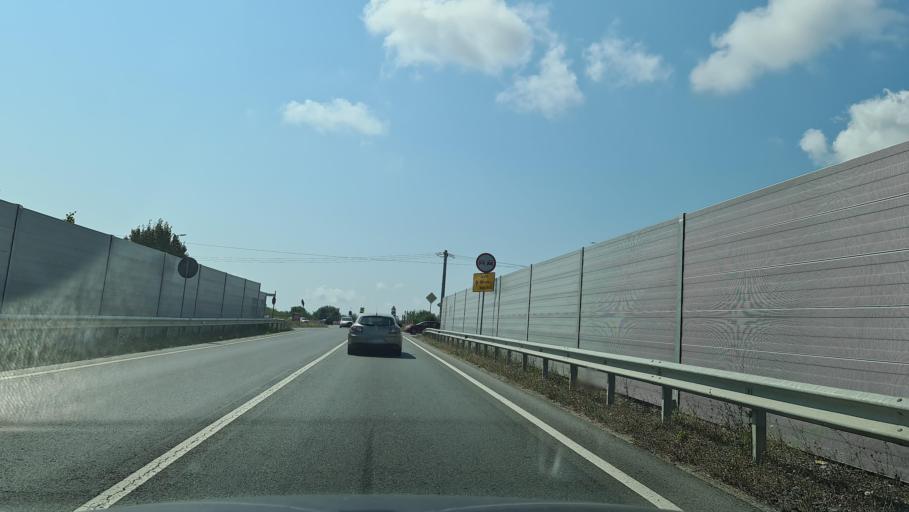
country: RO
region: Constanta
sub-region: Comuna Agigea
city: Agigea
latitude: 44.0936
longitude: 28.6386
